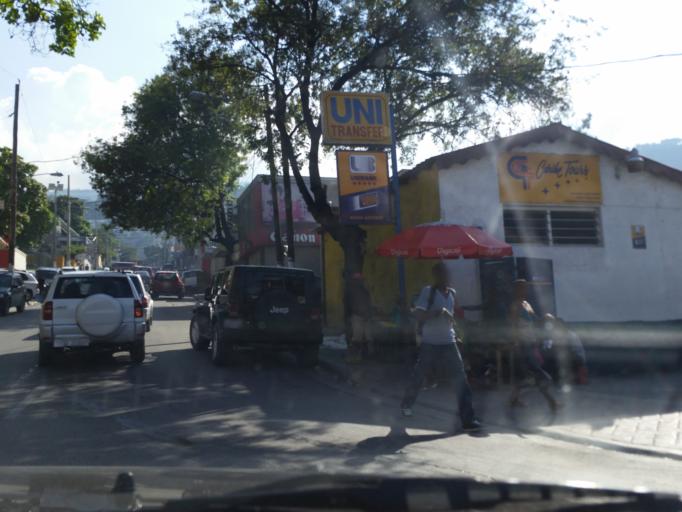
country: HT
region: Ouest
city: Petionville
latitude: 18.5168
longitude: -72.2895
